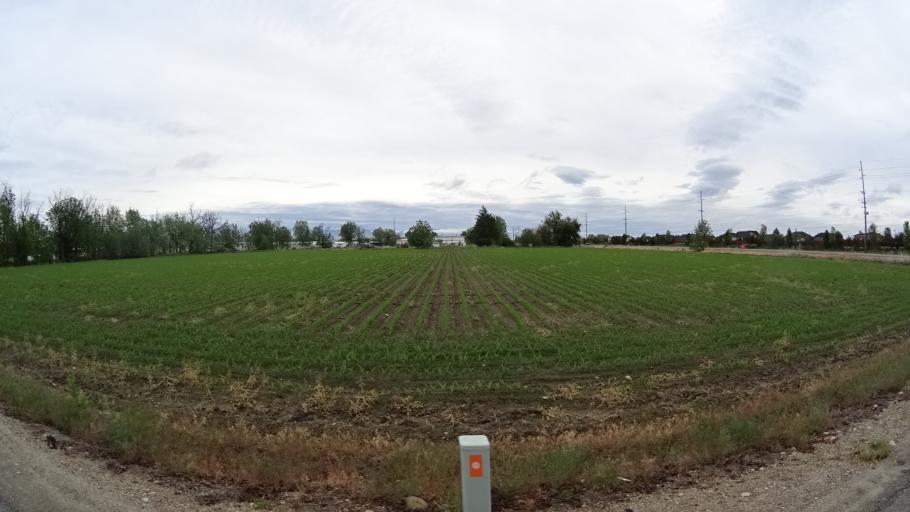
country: US
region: Idaho
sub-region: Ada County
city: Star
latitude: 43.6927
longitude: -116.4735
